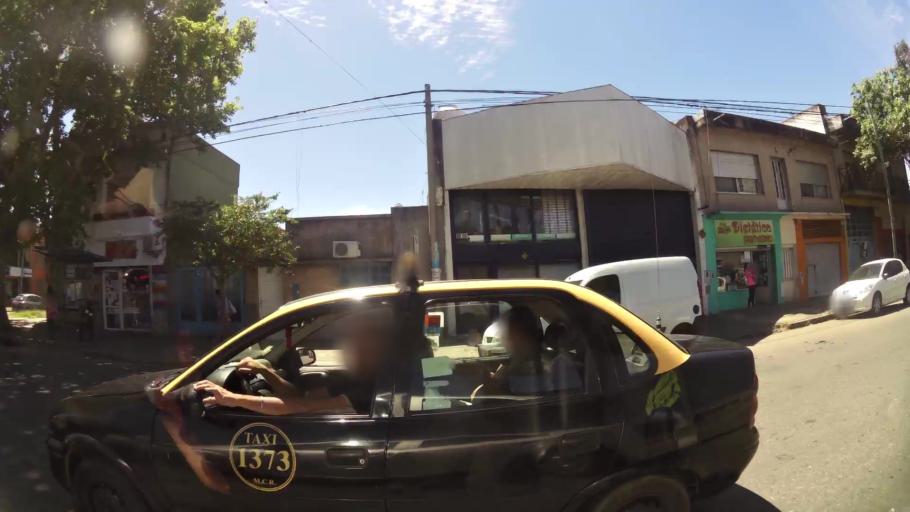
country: AR
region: Santa Fe
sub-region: Departamento de Rosario
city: Rosario
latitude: -32.9476
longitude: -60.7122
